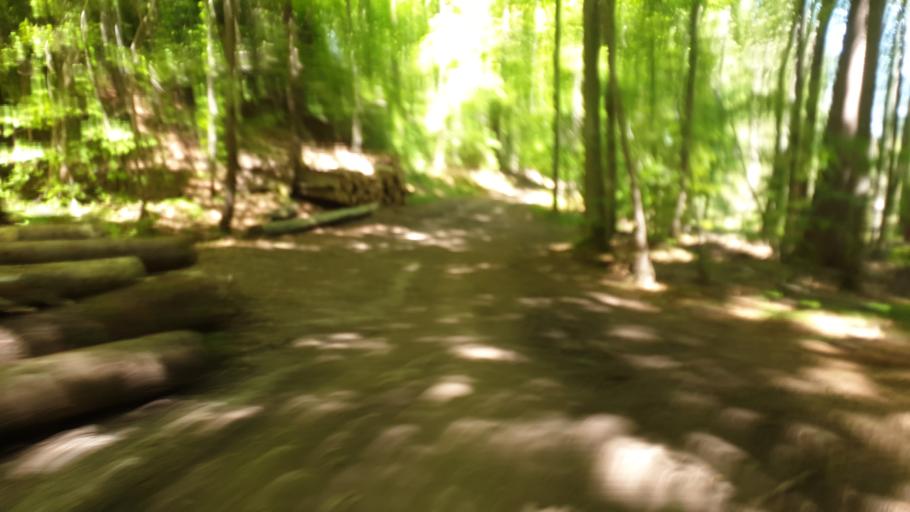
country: DE
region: Bavaria
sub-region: Upper Bavaria
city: Iffeldorf
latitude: 47.7828
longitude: 11.3001
